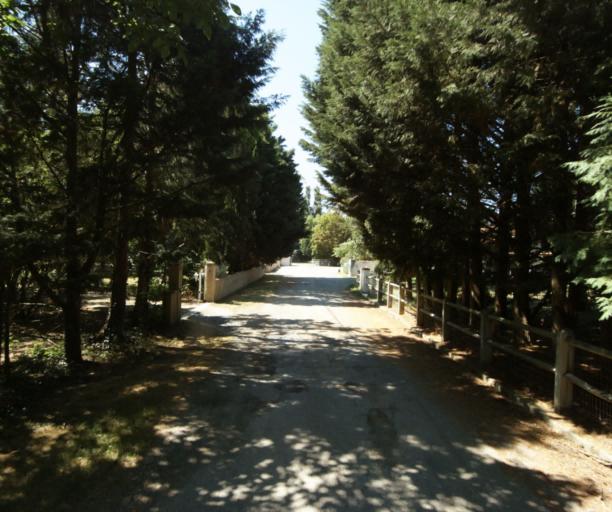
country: FR
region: Midi-Pyrenees
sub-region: Departement de la Haute-Garonne
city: Revel
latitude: 43.4713
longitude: 2.0086
